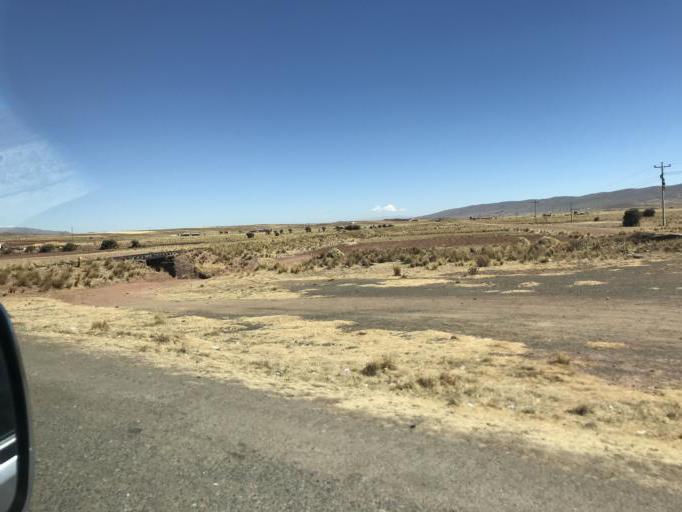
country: BO
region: La Paz
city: Tiahuanaco
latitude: -16.5936
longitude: -68.5725
